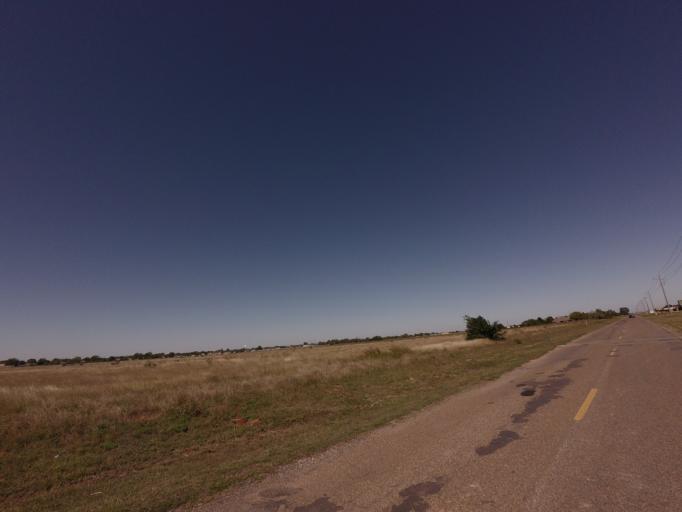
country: US
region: New Mexico
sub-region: Curry County
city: Clovis
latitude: 34.4210
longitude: -103.1608
